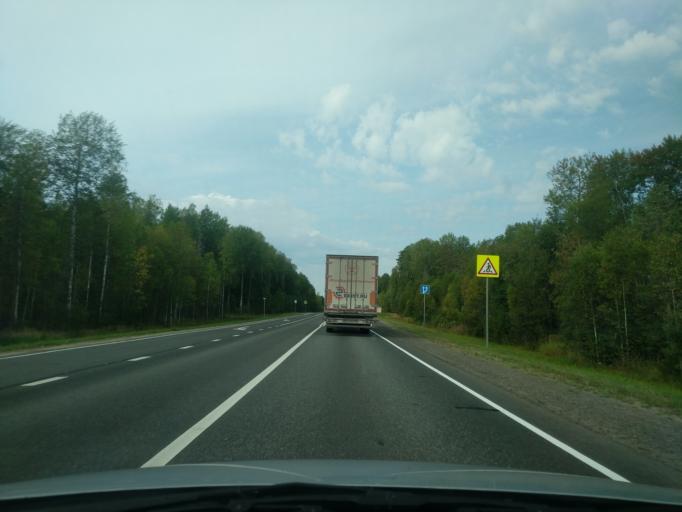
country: RU
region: Kirov
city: Leninskoye
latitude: 58.3189
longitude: 46.8702
